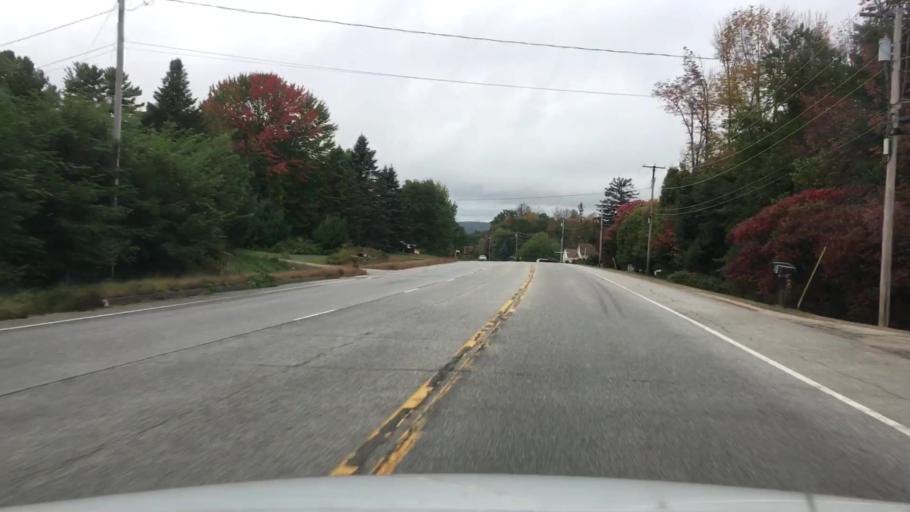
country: US
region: Maine
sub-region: Oxford County
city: Oxford
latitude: 44.1199
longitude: -70.4455
